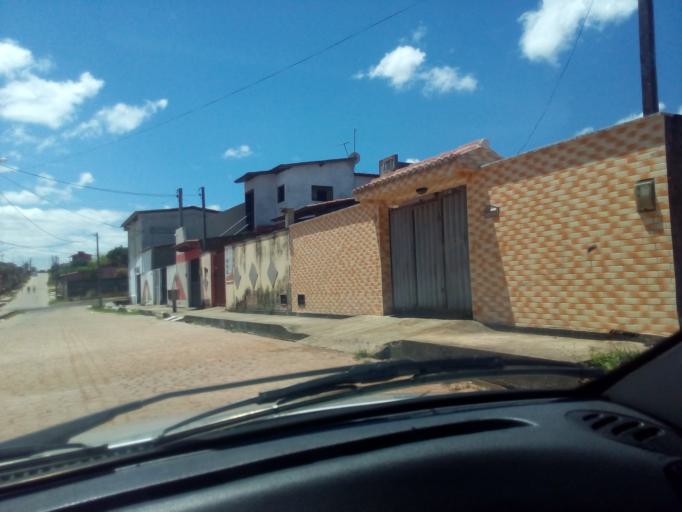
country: BR
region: Rio Grande do Norte
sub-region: Sao Goncalo Do Amarante
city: Sao Goncalo do Amarante
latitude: -5.7852
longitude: -35.3282
